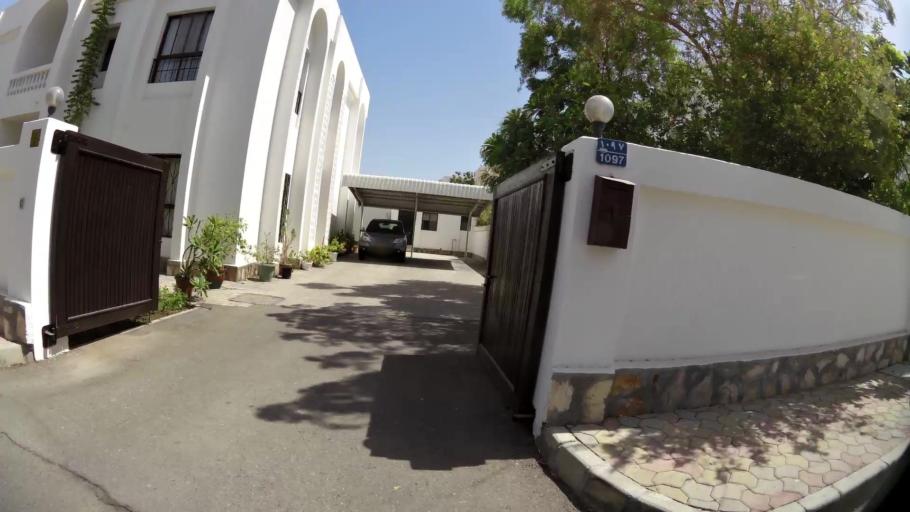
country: OM
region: Muhafazat Masqat
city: Bawshar
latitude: 23.5940
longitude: 58.4514
